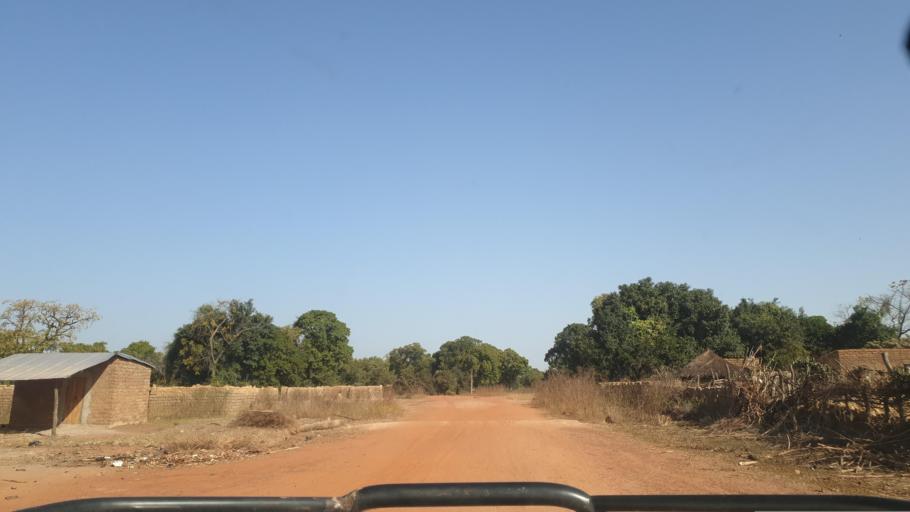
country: ML
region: Sikasso
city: Bougouni
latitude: 11.7697
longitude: -6.9025
